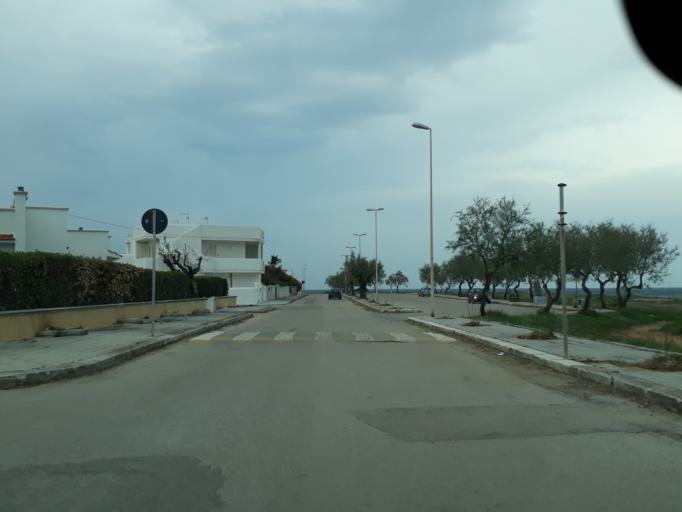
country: IT
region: Apulia
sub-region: Provincia di Brindisi
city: Carovigno
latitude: 40.7557
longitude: 17.7099
